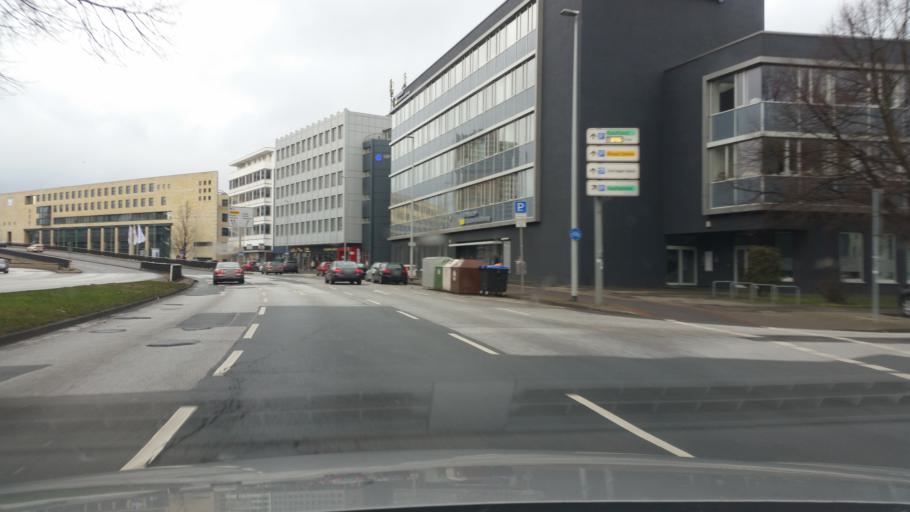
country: DE
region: Lower Saxony
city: Hannover
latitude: 52.3776
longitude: 9.7490
